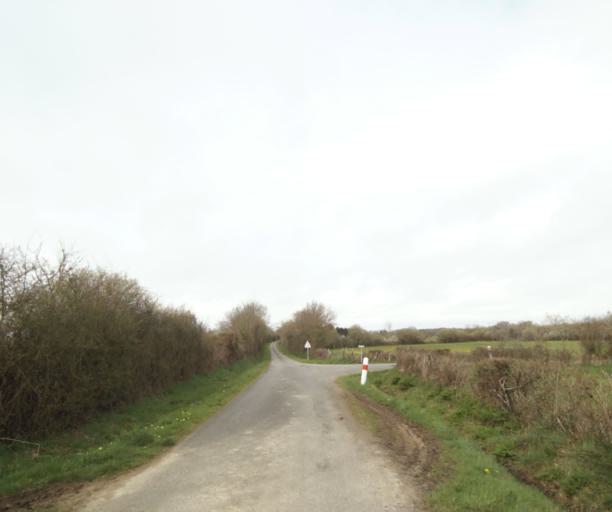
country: FR
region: Pays de la Loire
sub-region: Departement de la Loire-Atlantique
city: Bouvron
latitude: 47.4209
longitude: -1.8840
